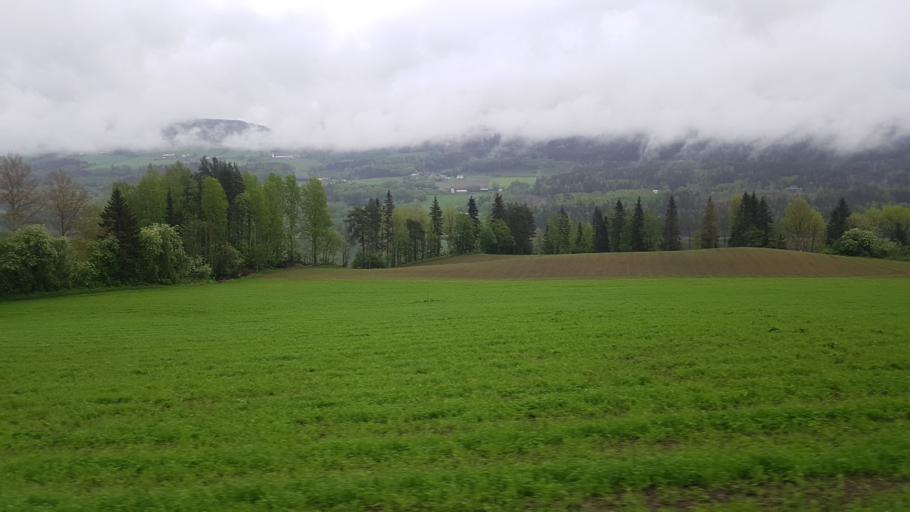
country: NO
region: Oppland
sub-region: Oyer
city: Tretten
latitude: 61.3357
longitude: 10.2849
